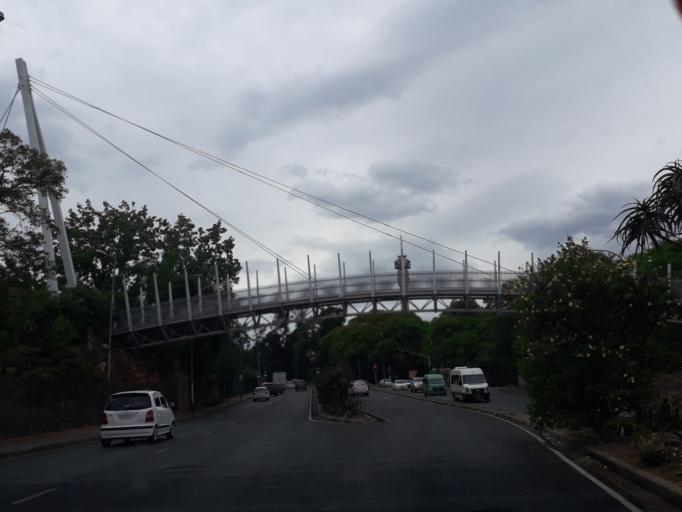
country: ZA
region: Gauteng
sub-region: City of Johannesburg Metropolitan Municipality
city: Johannesburg
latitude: -26.1761
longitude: 28.0519
